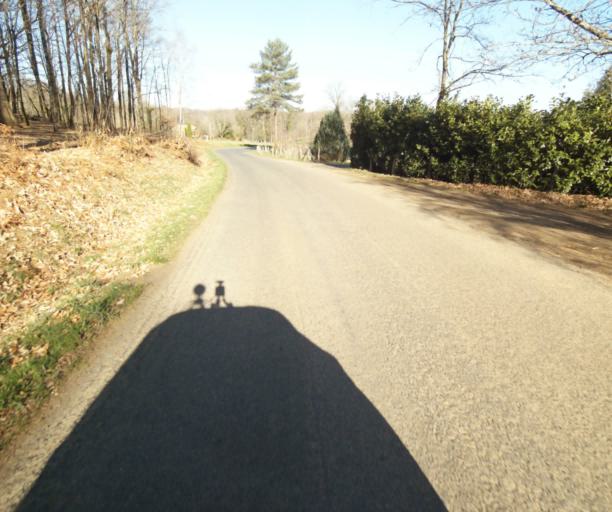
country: FR
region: Limousin
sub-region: Departement de la Correze
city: Saint-Clement
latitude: 45.3788
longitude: 1.6445
